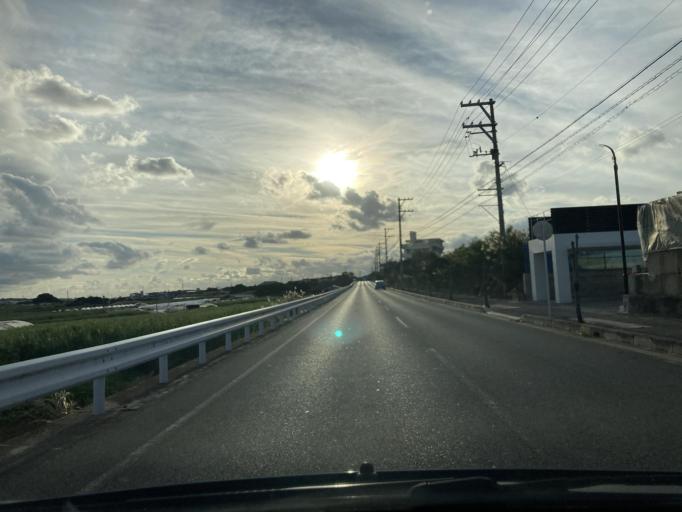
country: JP
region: Okinawa
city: Itoman
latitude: 26.1493
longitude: 127.6989
